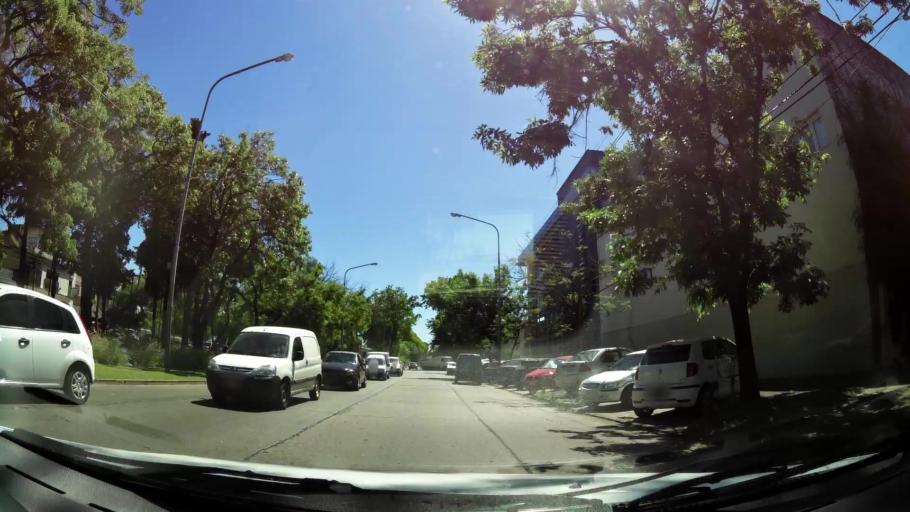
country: AR
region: Buenos Aires
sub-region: Partido de General San Martin
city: General San Martin
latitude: -34.5825
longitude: -58.5347
